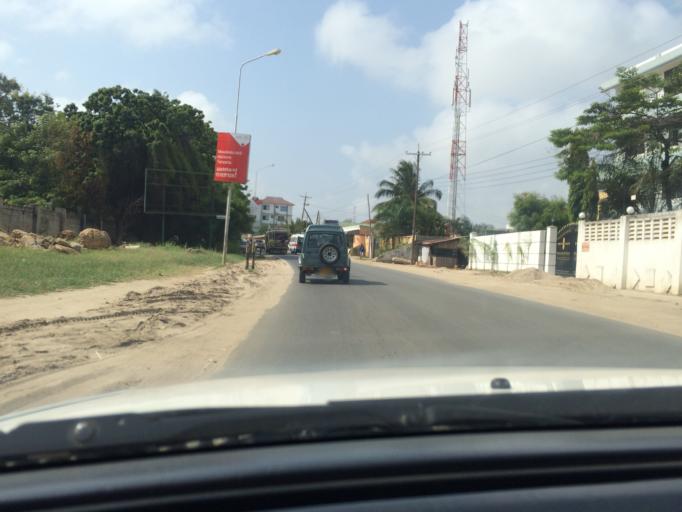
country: TZ
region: Dar es Salaam
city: Magomeni
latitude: -6.7635
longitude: 39.2695
